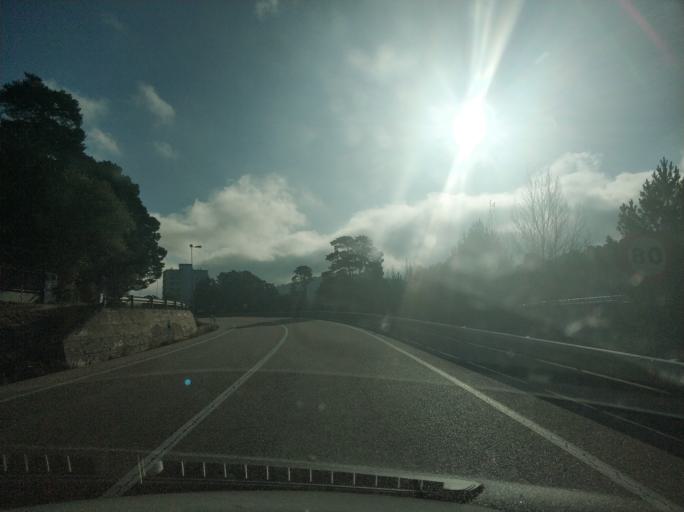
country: ES
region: Castille and Leon
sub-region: Provincia de Soria
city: Navaleno
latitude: 41.8382
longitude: -3.0156
